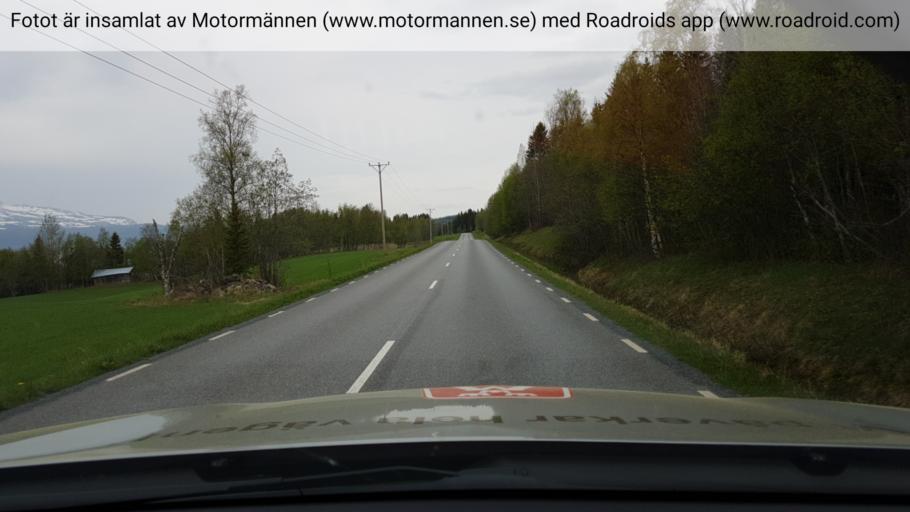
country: SE
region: Jaemtland
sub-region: Are Kommun
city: Jarpen
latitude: 63.4584
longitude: 13.3497
